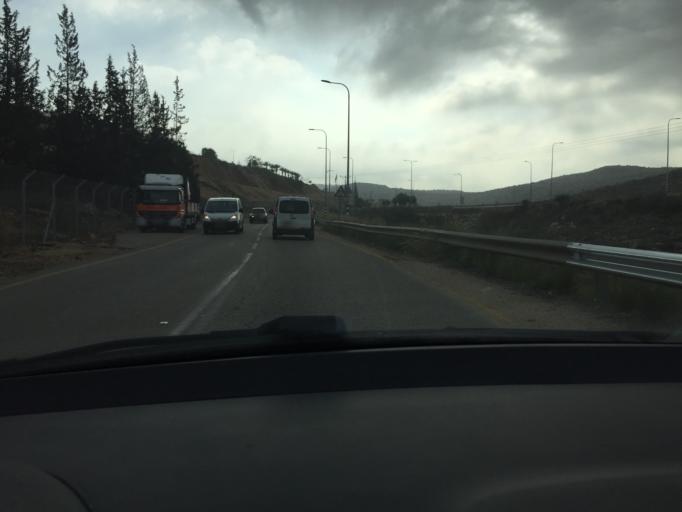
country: PS
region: West Bank
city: Al Lubban al Gharbi
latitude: 32.0344
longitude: 35.0472
